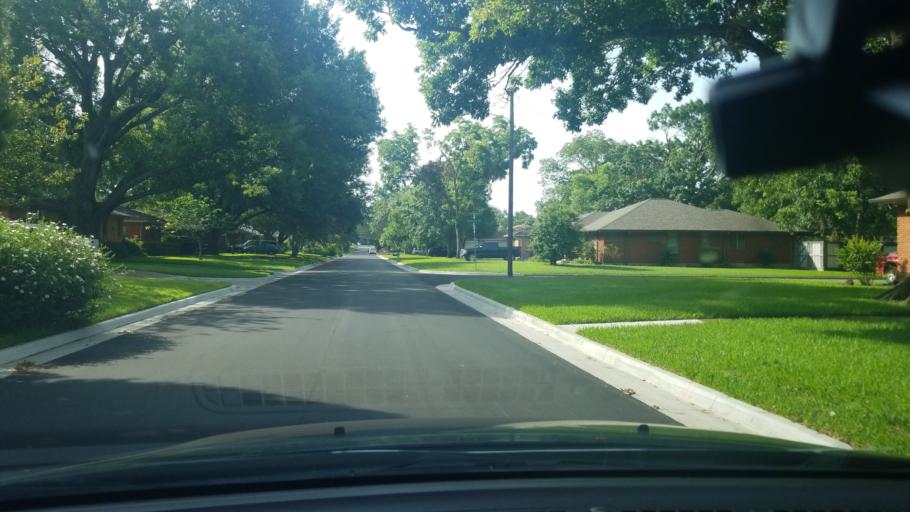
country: US
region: Texas
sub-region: Dallas County
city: Highland Park
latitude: 32.8045
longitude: -96.7059
